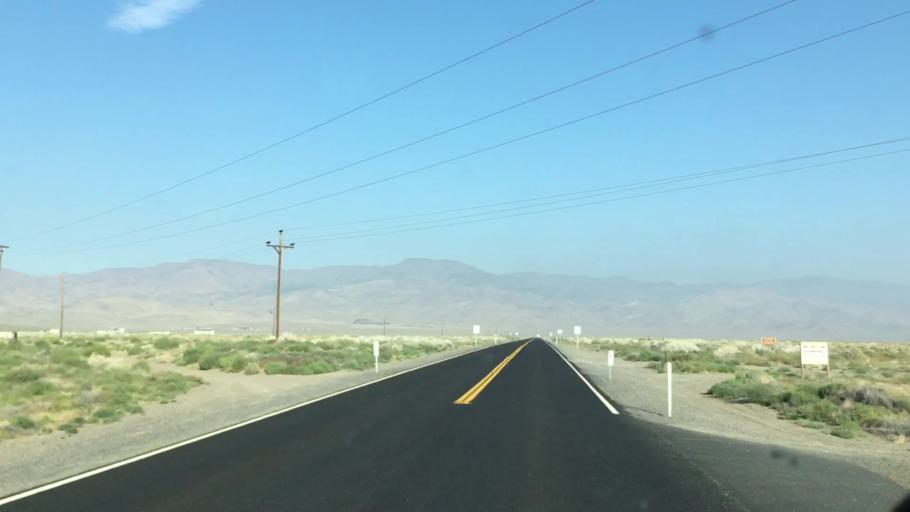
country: US
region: Nevada
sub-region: Lyon County
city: Fernley
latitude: 39.6410
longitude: -119.2990
